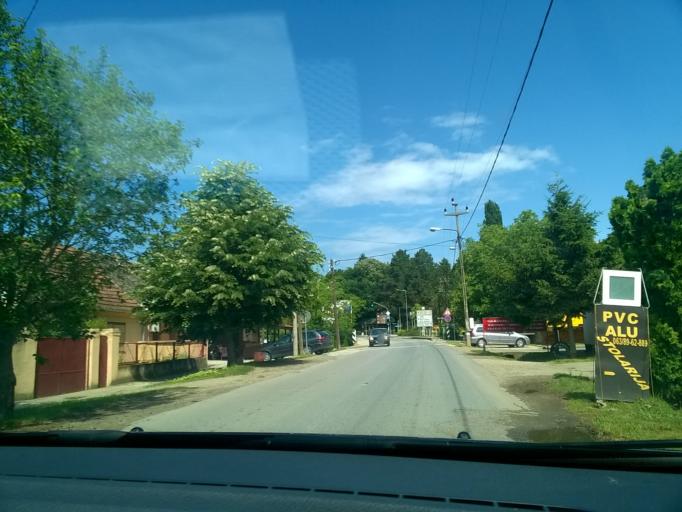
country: RS
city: Vrdnik
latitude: 45.1275
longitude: 19.7884
